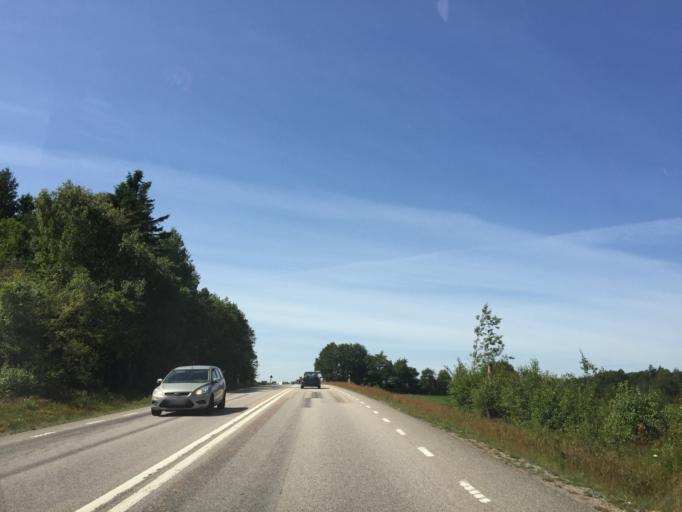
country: SE
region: Vaestra Goetaland
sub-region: Lysekils Kommun
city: Lysekil
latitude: 58.3062
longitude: 11.4836
